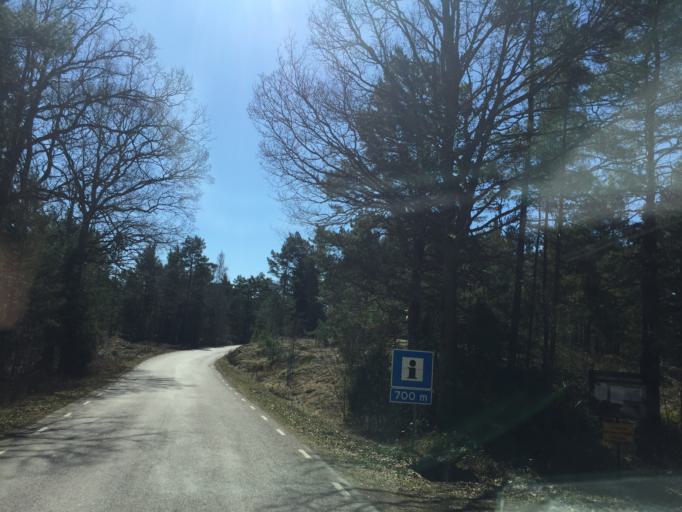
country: SE
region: Kalmar
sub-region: Oskarshamns Kommun
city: Oskarshamn
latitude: 57.2360
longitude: 16.4797
